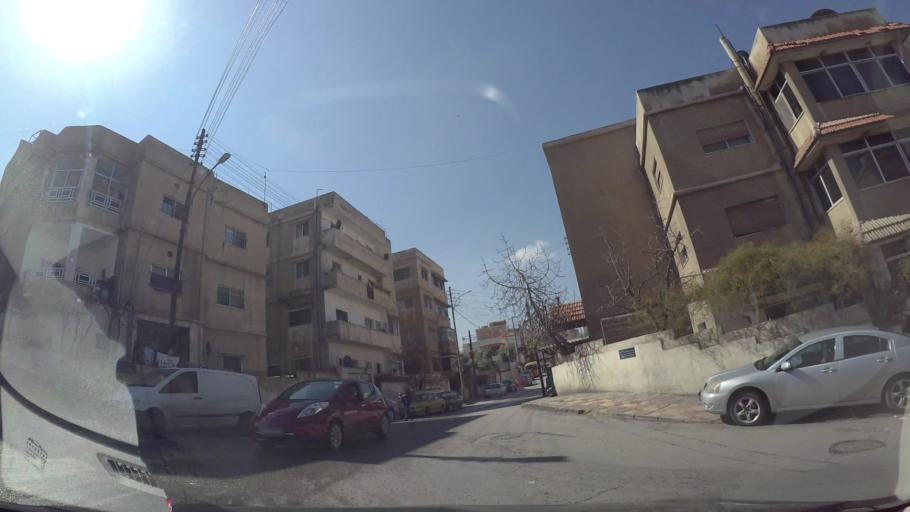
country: JO
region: Amman
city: Amman
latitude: 31.9807
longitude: 35.9843
